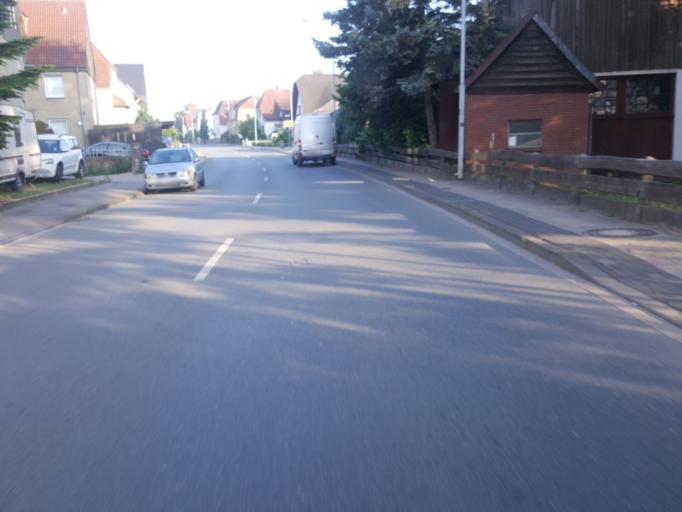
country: DE
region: North Rhine-Westphalia
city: Buende
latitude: 52.1998
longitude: 8.5961
